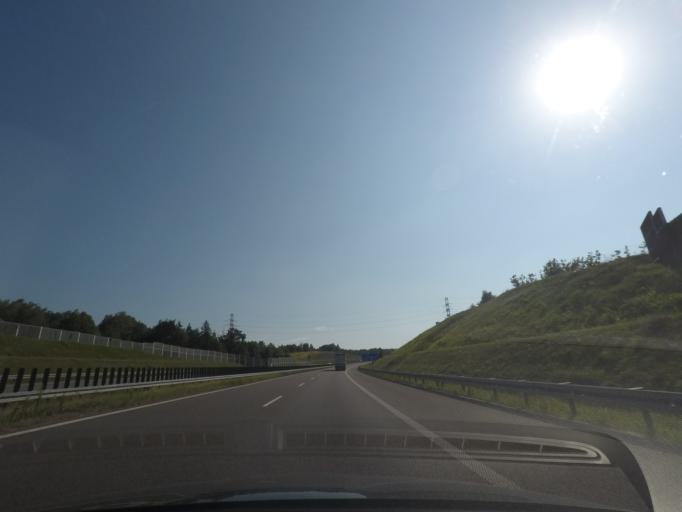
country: PL
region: Silesian Voivodeship
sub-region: Powiat wodzislawski
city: Mszana
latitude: 49.9649
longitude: 18.5344
